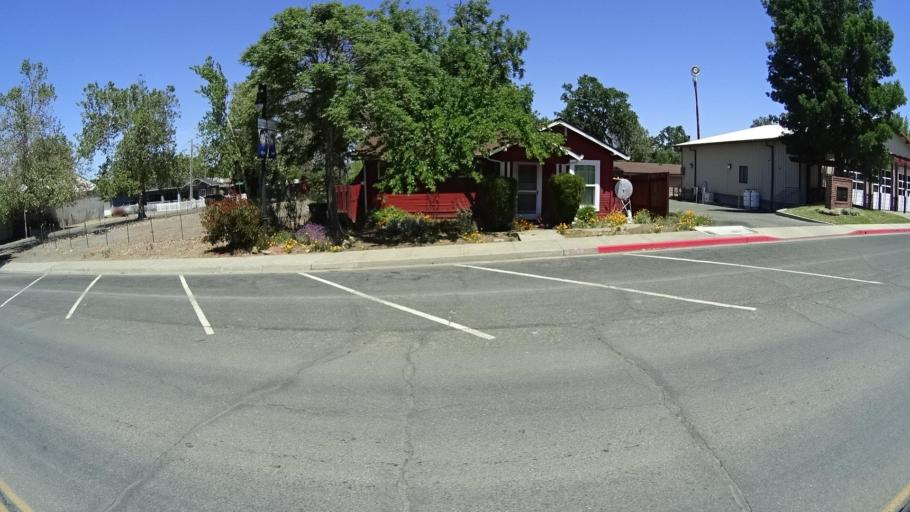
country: US
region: California
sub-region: Lake County
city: Lower Lake
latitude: 38.9103
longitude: -122.6072
